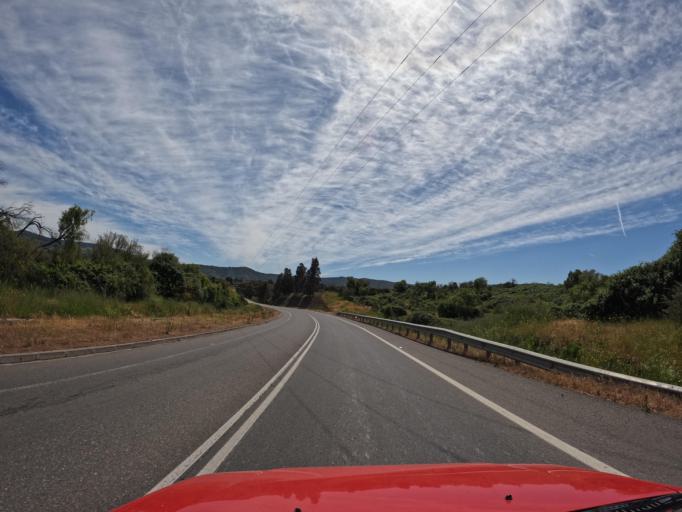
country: CL
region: Maule
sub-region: Provincia de Talca
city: Talca
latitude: -35.2811
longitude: -71.5315
